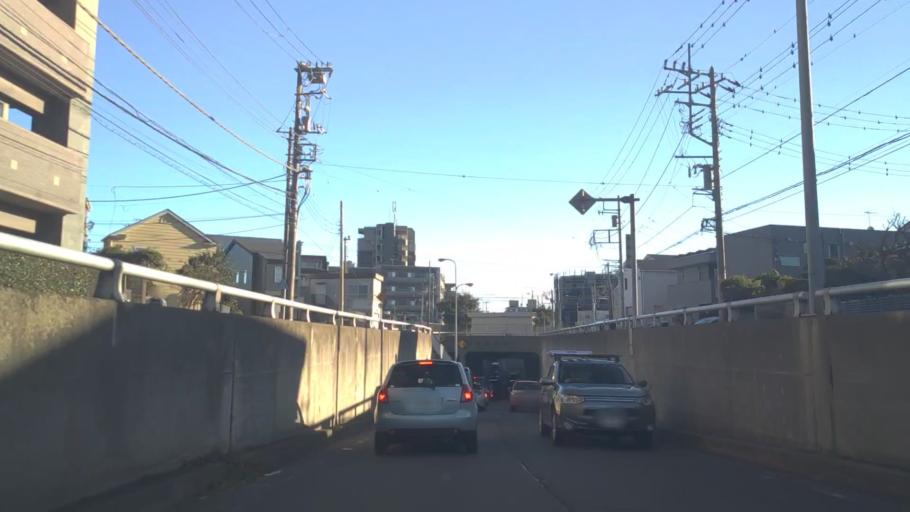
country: JP
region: Kanagawa
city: Chigasaki
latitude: 35.3341
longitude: 139.4149
